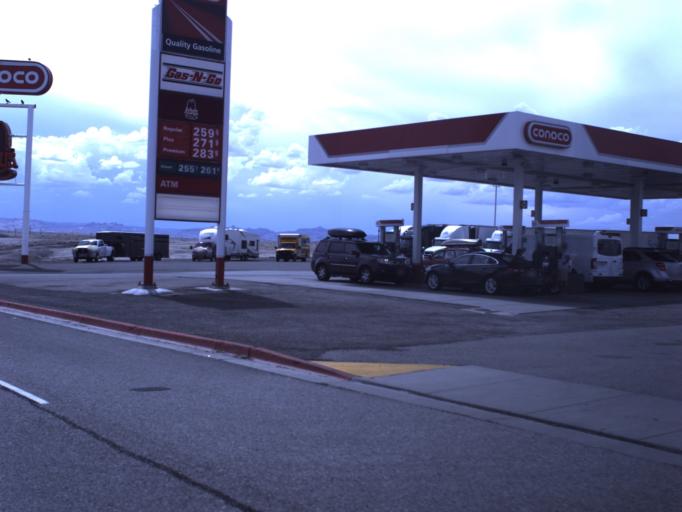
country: US
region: Utah
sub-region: Carbon County
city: East Carbon City
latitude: 38.9947
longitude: -110.1845
